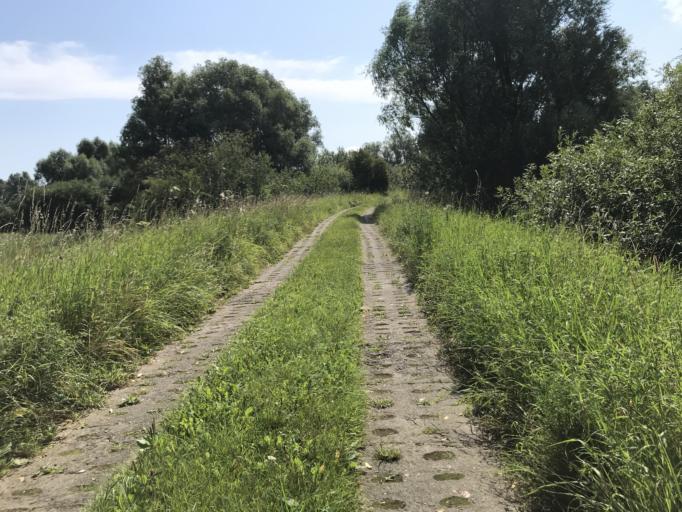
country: PL
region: Pomeranian Voivodeship
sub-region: Gdansk
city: Gdansk
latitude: 54.3239
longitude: 18.6656
